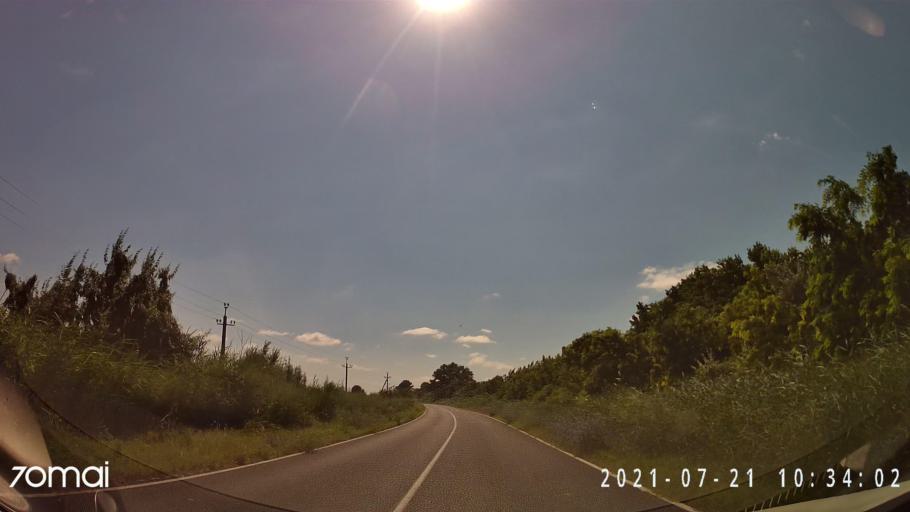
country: RO
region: Tulcea
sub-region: Oras Isaccea
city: Isaccea
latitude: 45.2972
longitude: 28.4400
